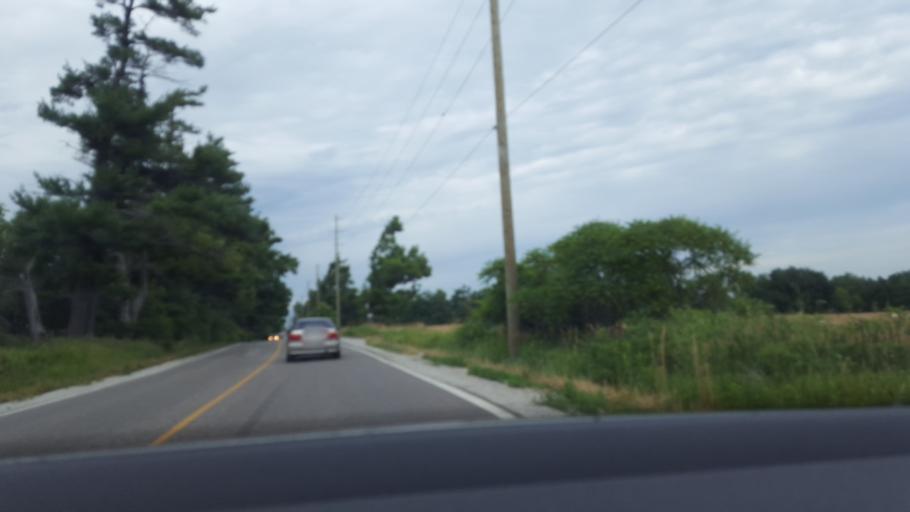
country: CA
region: Ontario
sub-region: Halton
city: Milton
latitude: 43.5836
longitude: -79.8727
